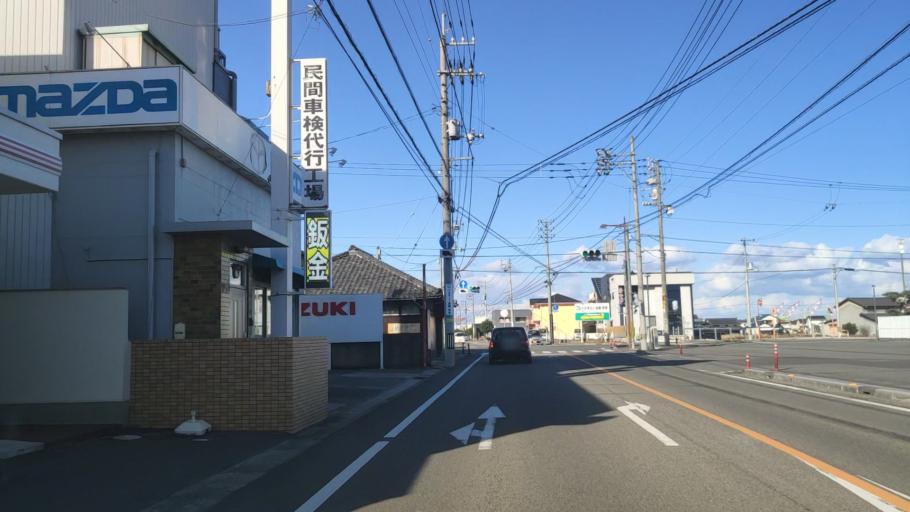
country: JP
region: Ehime
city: Saijo
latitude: 33.9210
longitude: 133.1918
